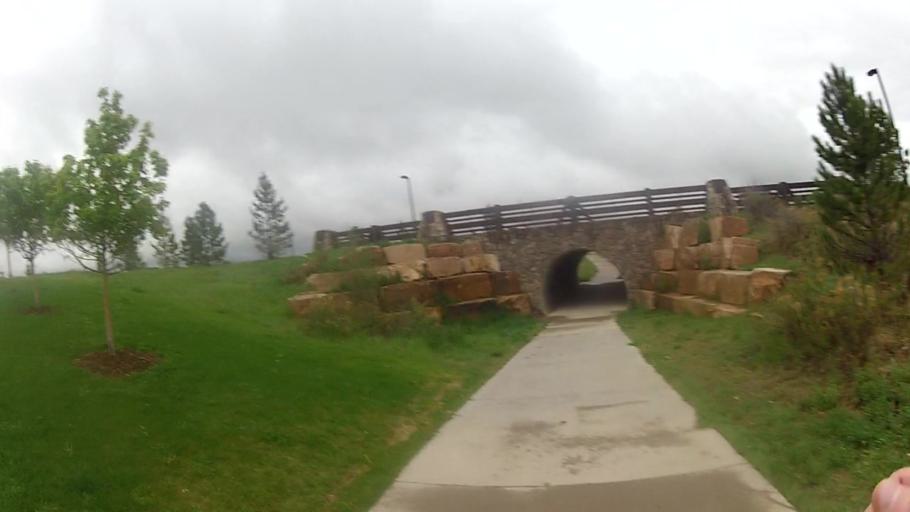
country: US
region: Colorado
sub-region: Larimer County
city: Fort Collins
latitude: 40.5385
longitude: -105.1258
